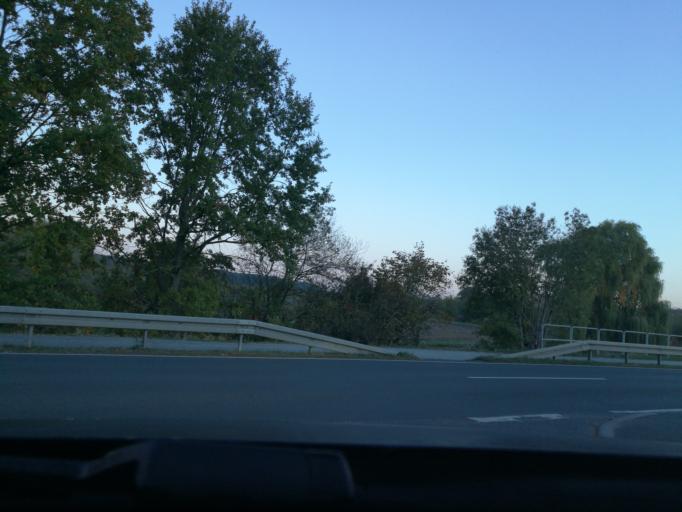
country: DE
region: Bavaria
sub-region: Regierungsbezirk Mittelfranken
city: Veitsbronn
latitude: 49.5172
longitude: 10.8970
